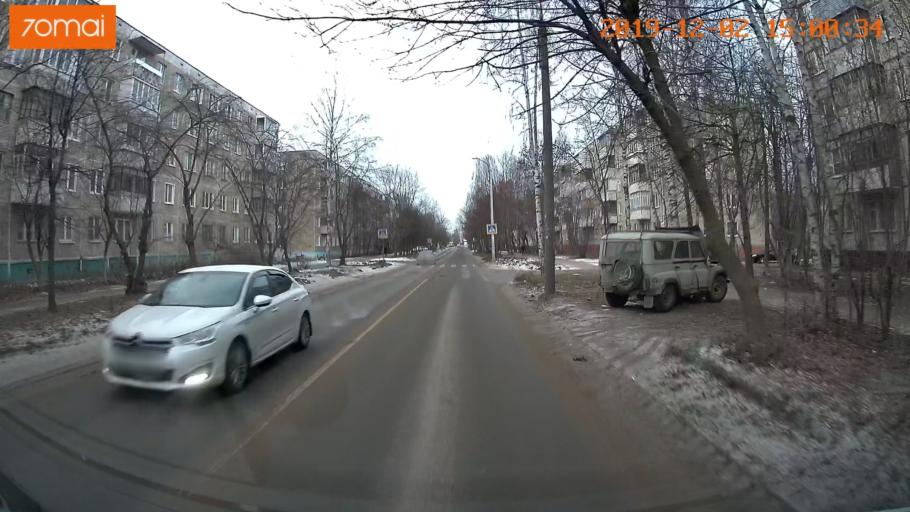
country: RU
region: Ivanovo
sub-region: Gorod Ivanovo
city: Ivanovo
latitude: 56.9709
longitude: 41.0033
